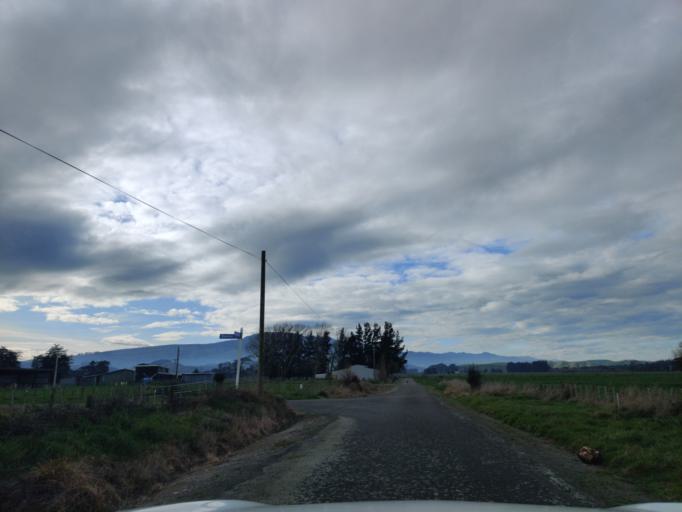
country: NZ
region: Manawatu-Wanganui
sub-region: Palmerston North City
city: Palmerston North
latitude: -40.3329
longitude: 175.8565
